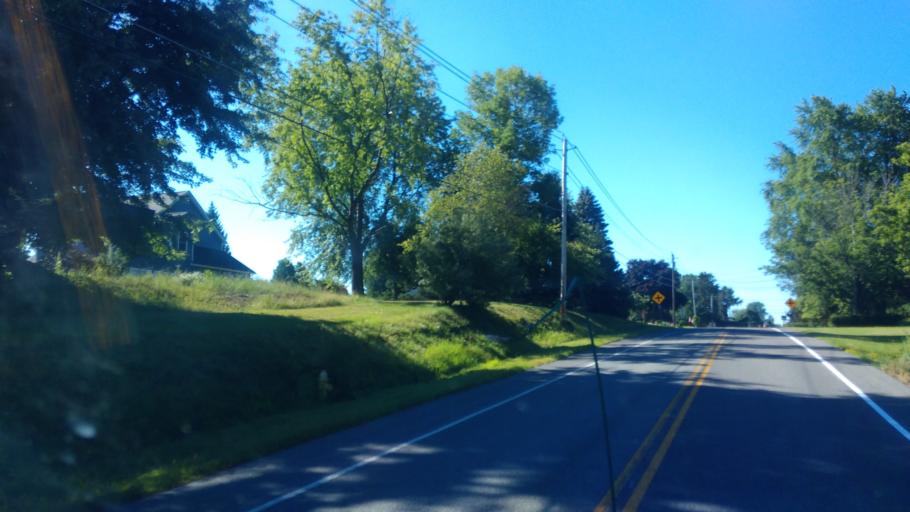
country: US
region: New York
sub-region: Monroe County
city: Webster
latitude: 43.2385
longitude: -77.4683
